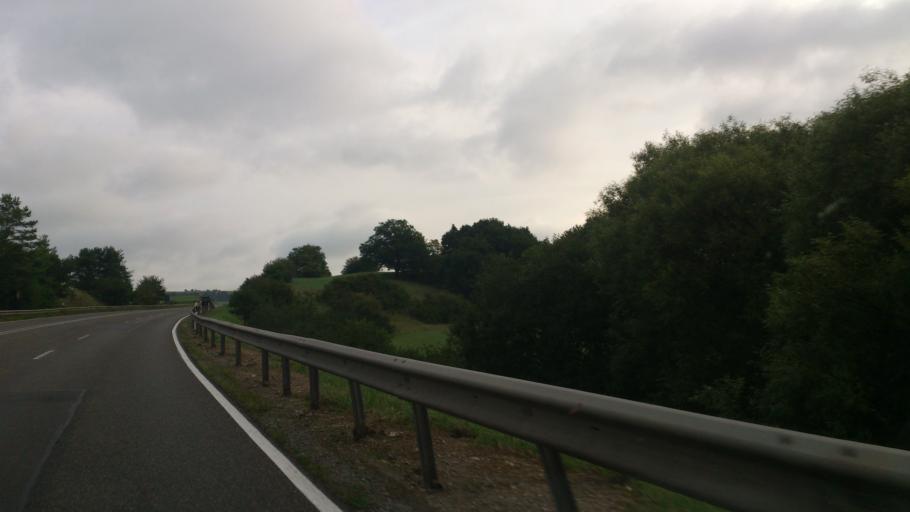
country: DE
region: Rheinland-Pfalz
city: Uxheim
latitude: 50.4035
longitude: 6.7345
